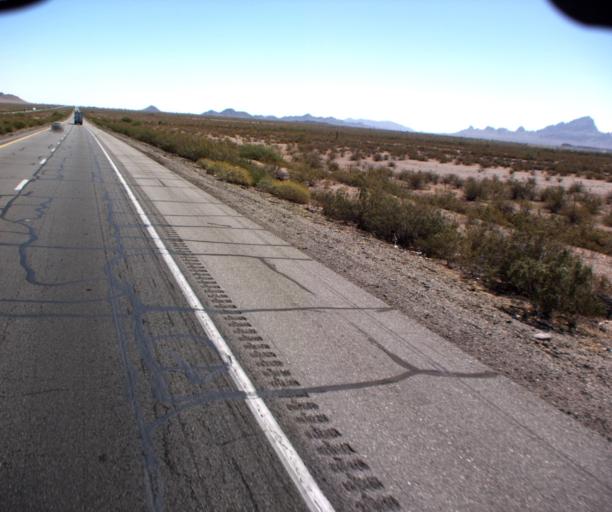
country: US
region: Arizona
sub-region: Maricopa County
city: Buckeye
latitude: 33.5268
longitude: -113.1082
